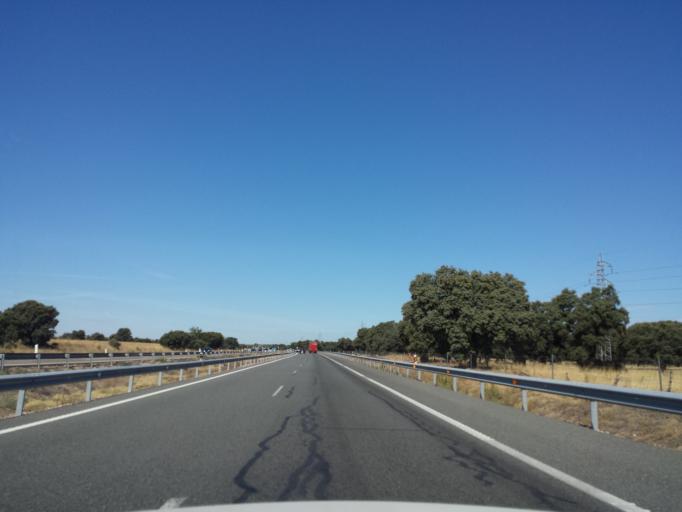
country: ES
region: Castille-La Mancha
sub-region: Province of Toledo
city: Alcanizo
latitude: 39.9232
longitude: -5.0906
